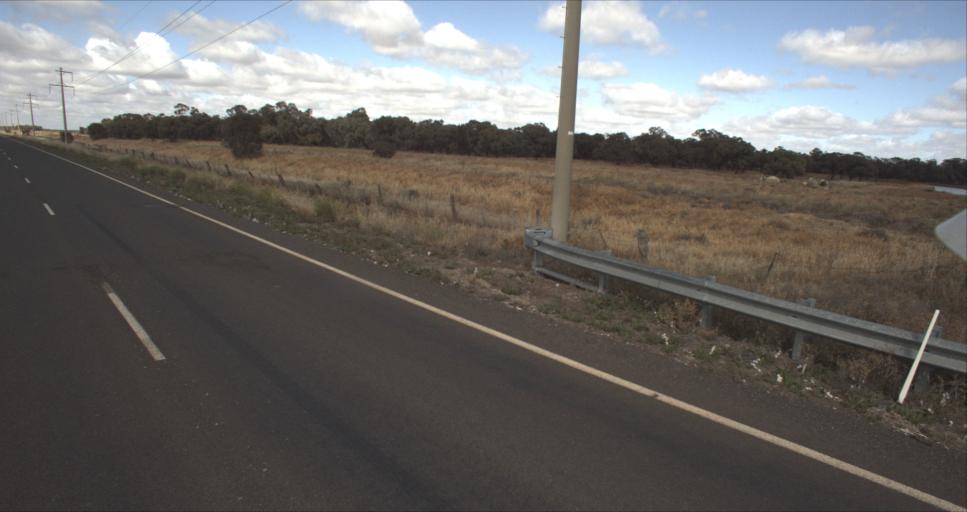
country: AU
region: New South Wales
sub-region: Murrumbidgee Shire
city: Darlington Point
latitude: -34.5414
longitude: 146.1721
